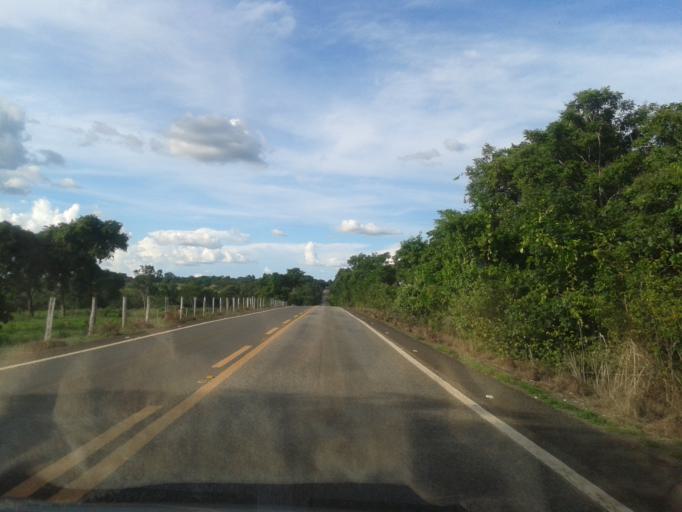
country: BR
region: Goias
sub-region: Crixas
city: Crixas
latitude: -13.9874
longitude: -50.3232
